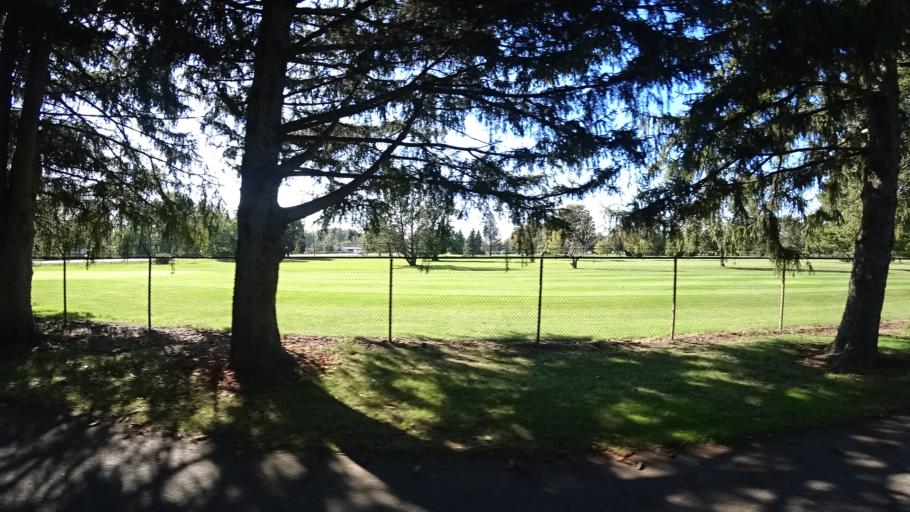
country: US
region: Indiana
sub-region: LaPorte County
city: Trail Creek
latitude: 41.7029
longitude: -86.8430
